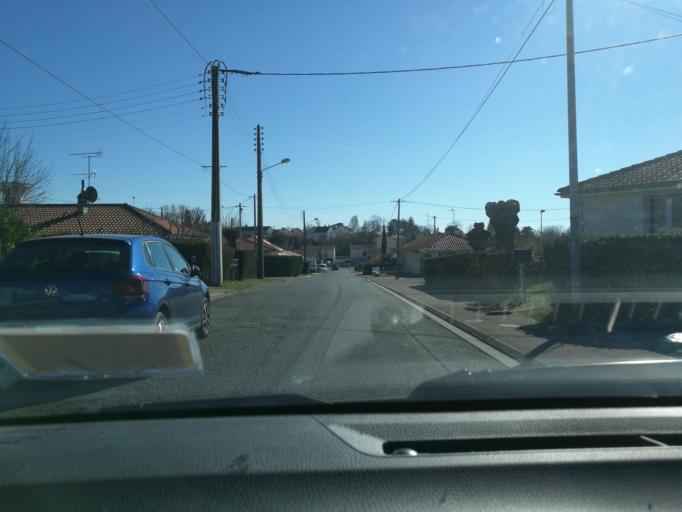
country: FR
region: Centre
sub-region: Departement du Loiret
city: Saint-Jean-de-la-Ruelle
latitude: 47.9010
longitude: 1.8656
